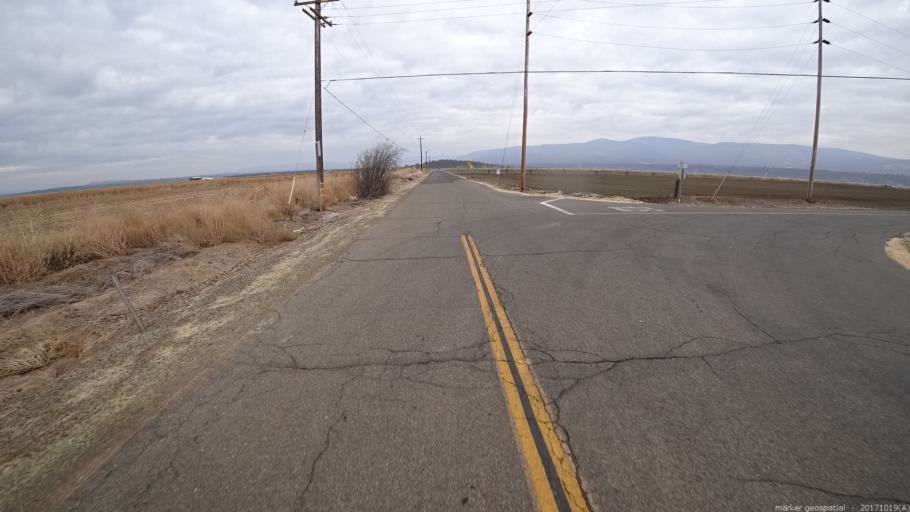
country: US
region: California
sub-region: Shasta County
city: Burney
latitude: 41.0767
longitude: -121.3652
